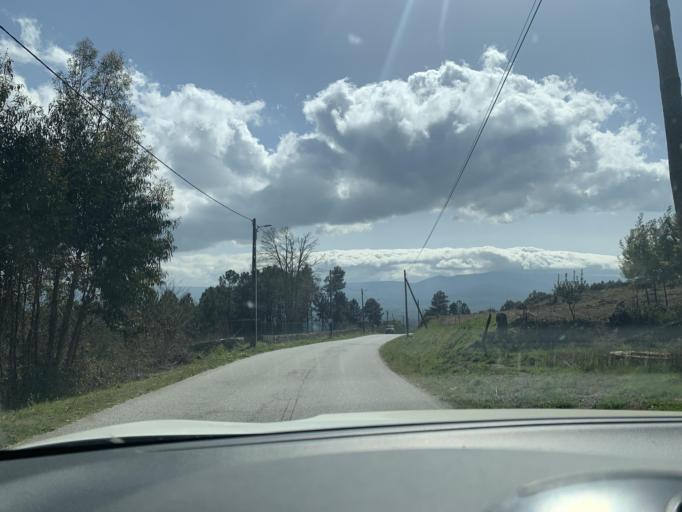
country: PT
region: Guarda
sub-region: Fornos de Algodres
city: Fornos de Algodres
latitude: 40.6101
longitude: -7.6049
